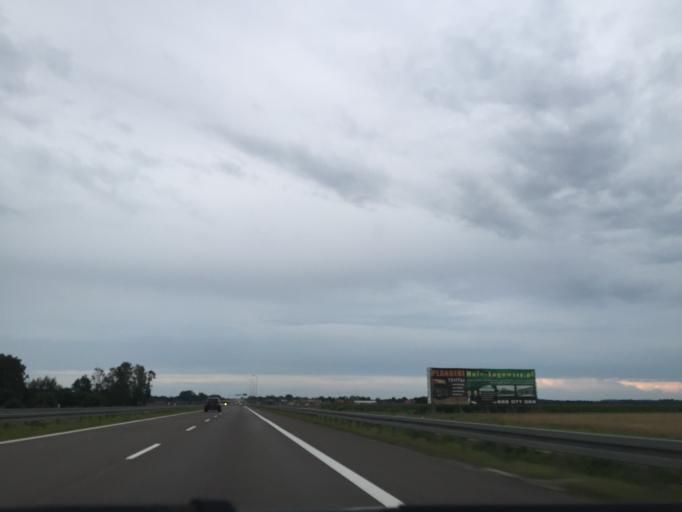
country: PL
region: Podlasie
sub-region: Powiat bialostocki
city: Tykocin
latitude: 53.1522
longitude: 22.8482
